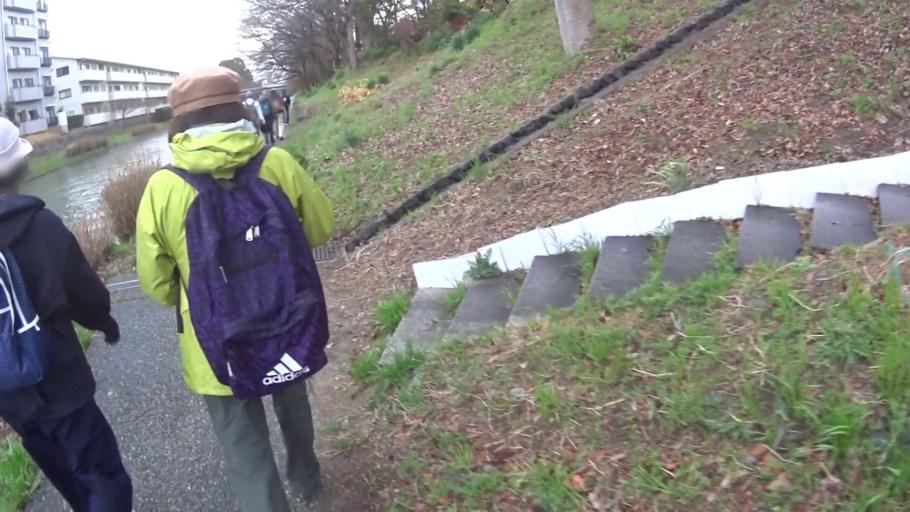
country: JP
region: Kyoto
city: Uji
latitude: 34.9296
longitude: 135.7555
